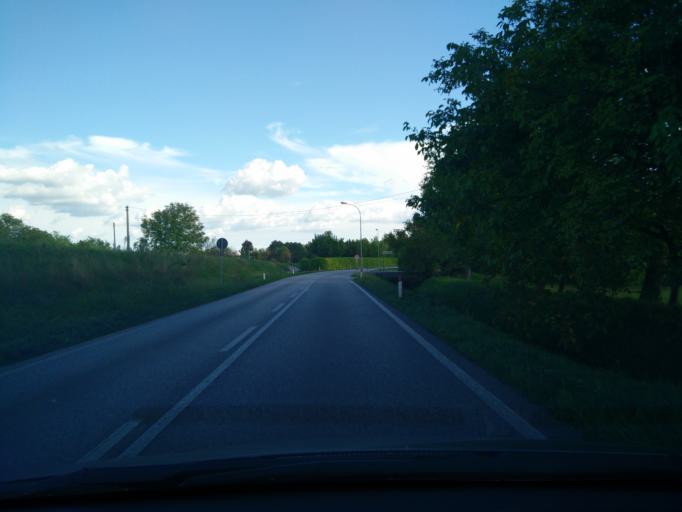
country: IT
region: Veneto
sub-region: Provincia di Treviso
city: Breda
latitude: 45.7431
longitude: 12.3468
